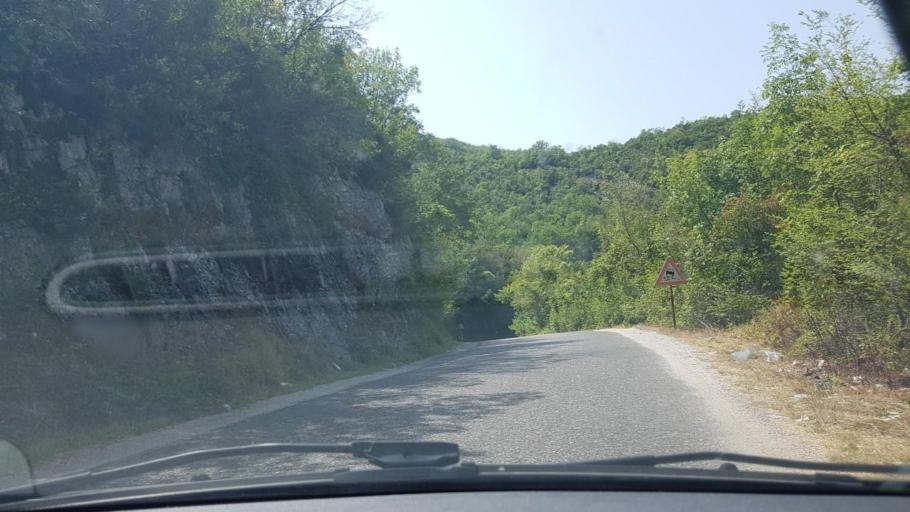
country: BA
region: Federation of Bosnia and Herzegovina
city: Tasovcici
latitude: 43.0099
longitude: 17.7920
